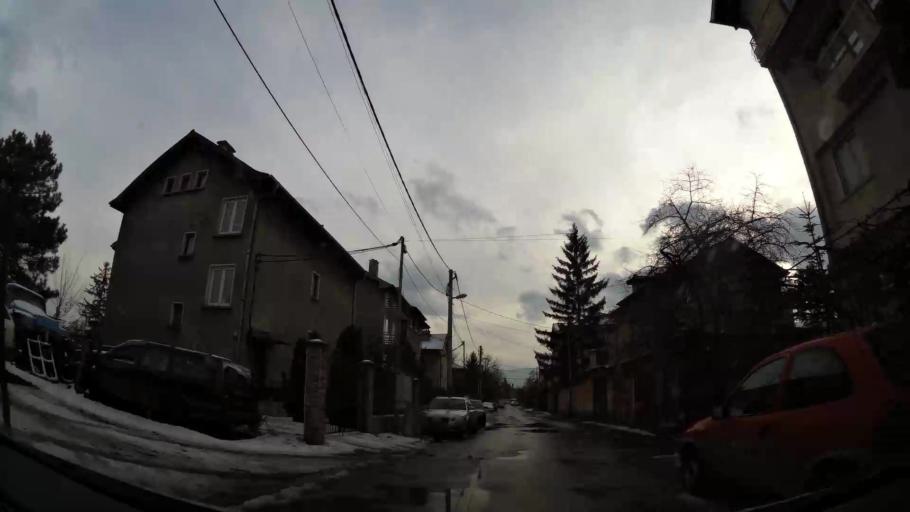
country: BG
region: Sofia-Capital
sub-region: Stolichna Obshtina
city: Sofia
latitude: 42.7249
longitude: 23.3320
